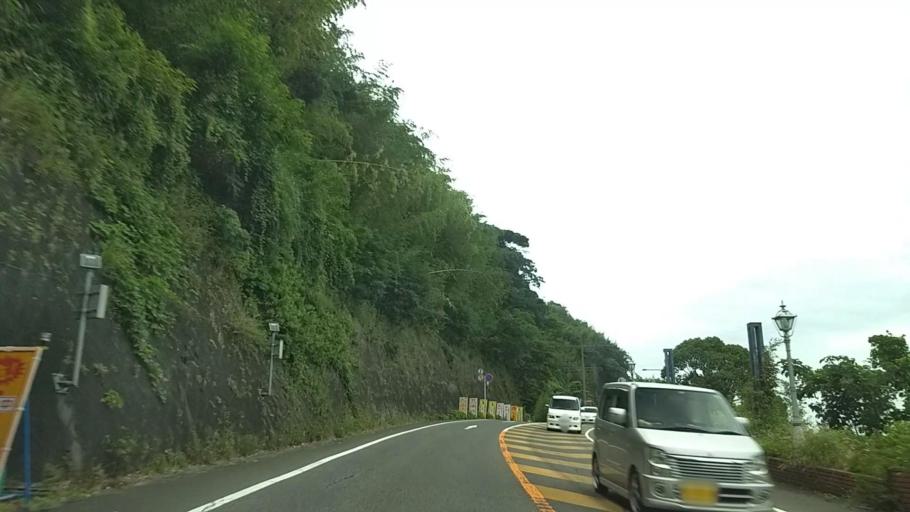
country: JP
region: Shizuoka
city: Atami
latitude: 35.0820
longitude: 139.0741
